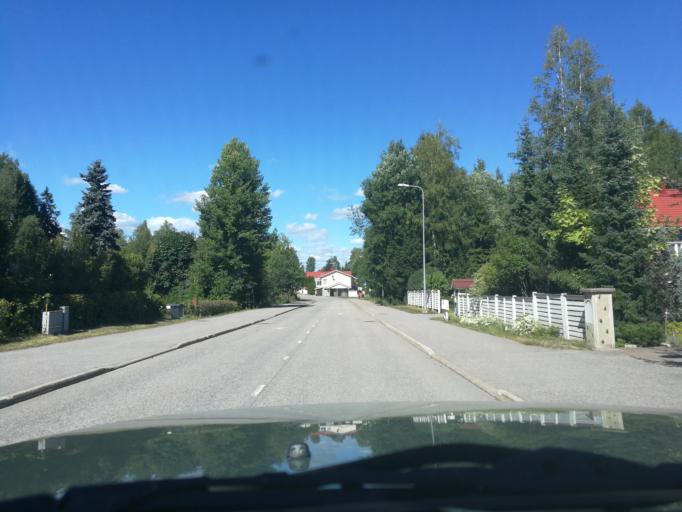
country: FI
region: Uusimaa
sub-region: Helsinki
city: Kerava
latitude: 60.3498
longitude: 25.1139
